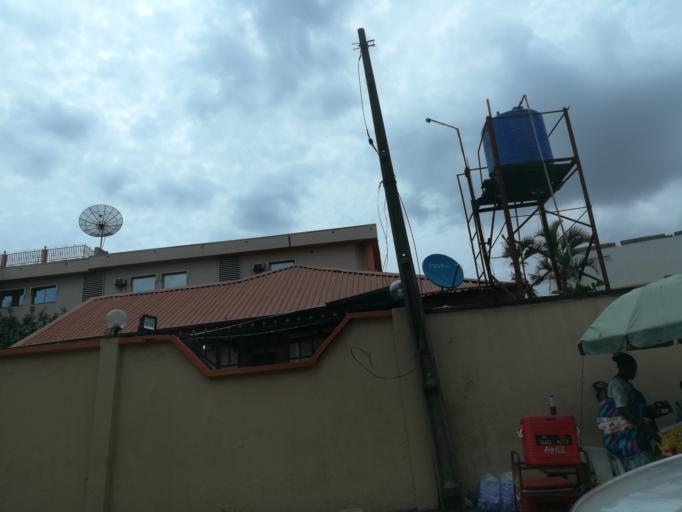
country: NG
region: Lagos
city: Ojota
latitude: 6.5738
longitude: 3.3673
